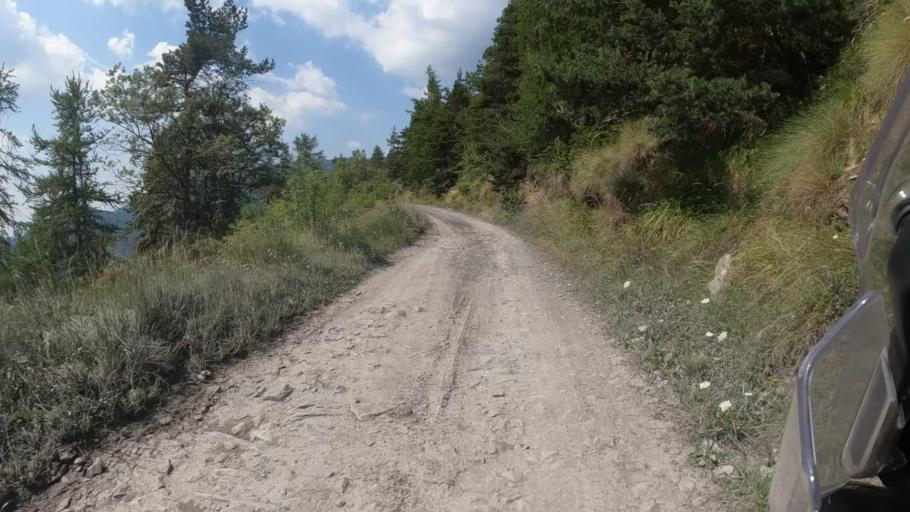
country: IT
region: Piedmont
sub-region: Provincia di Cuneo
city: Briga Alta
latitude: 44.0380
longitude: 7.6878
